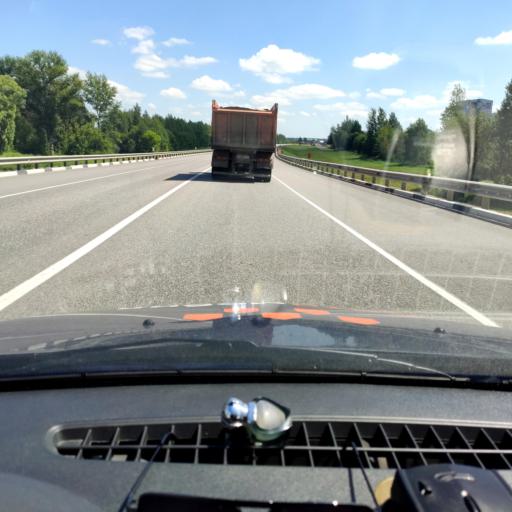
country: RU
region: Orjol
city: Orel
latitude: 52.8477
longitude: 36.2509
